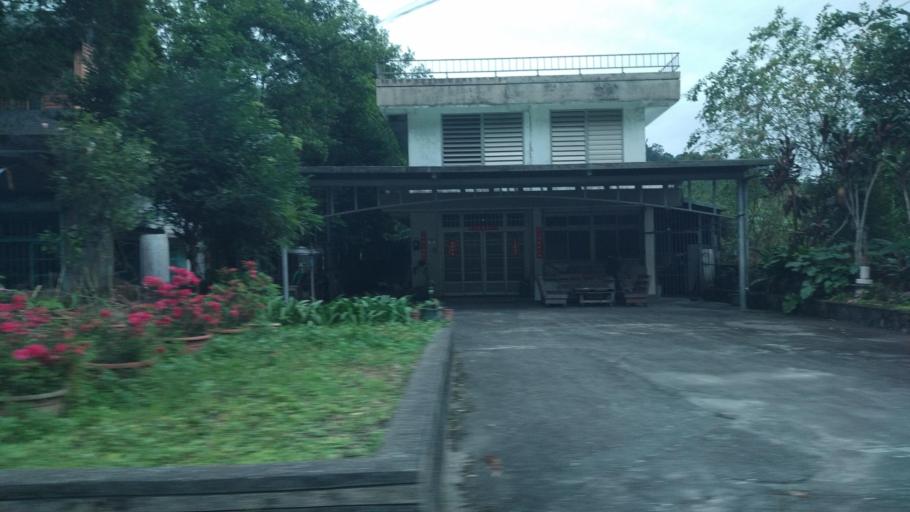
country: TW
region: Taiwan
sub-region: Hualien
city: Hualian
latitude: 23.9221
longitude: 121.5043
